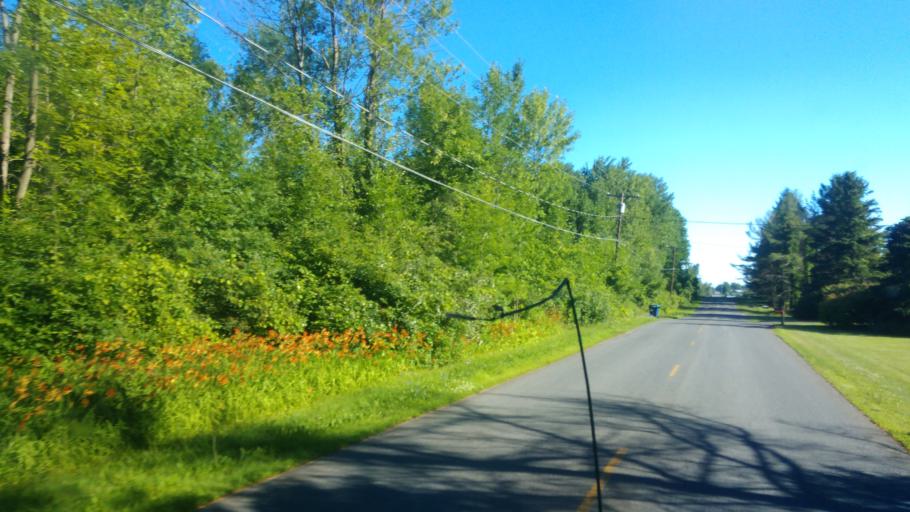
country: US
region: New York
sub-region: Wayne County
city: Sodus
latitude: 43.2666
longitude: -77.1128
